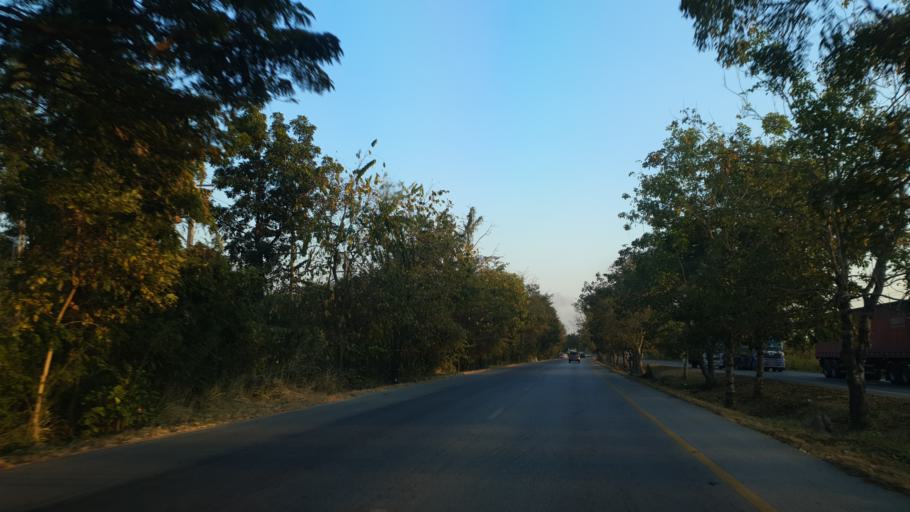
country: TH
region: Nakhon Sawan
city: Banphot Phisai
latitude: 15.9031
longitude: 99.8931
